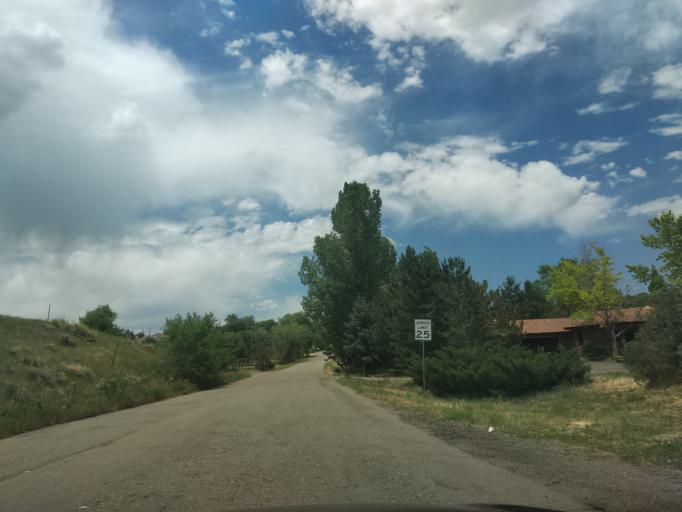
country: US
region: Colorado
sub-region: Jefferson County
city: Lakewood
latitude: 39.6701
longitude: -105.1067
